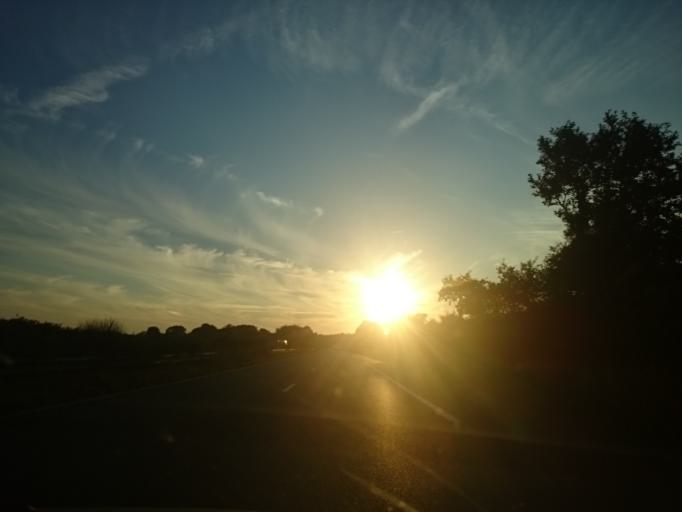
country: FR
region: Brittany
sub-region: Departement du Finistere
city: Le Trevoux
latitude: 47.8775
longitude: -3.6456
